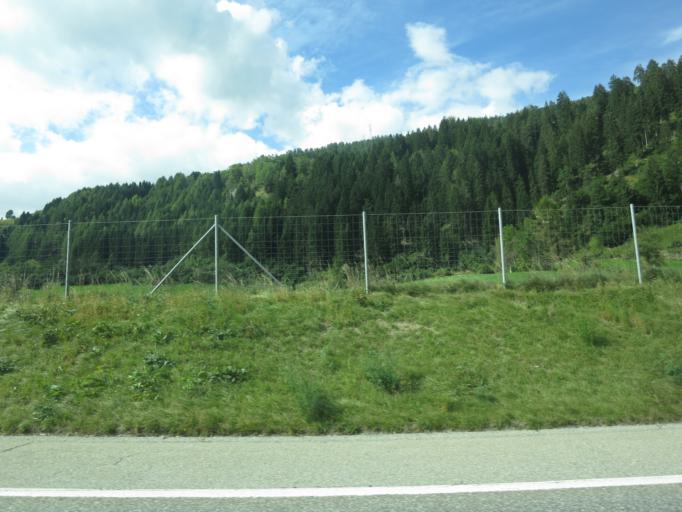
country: CH
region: Grisons
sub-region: Hinterrhein District
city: Thusis
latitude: 46.6396
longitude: 9.4408
